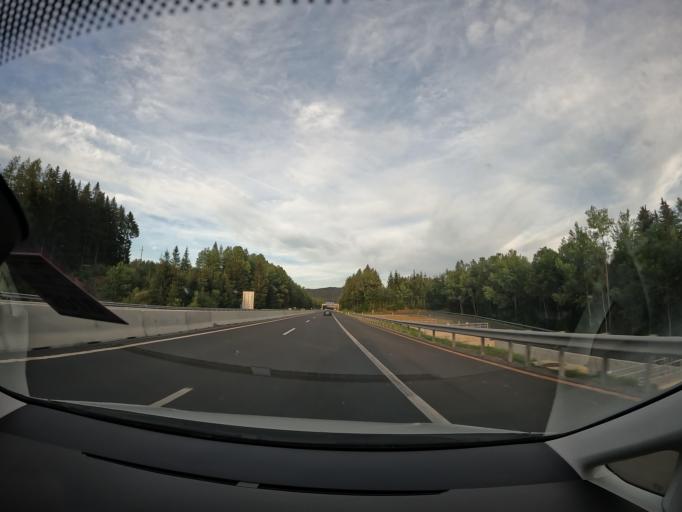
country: AT
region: Carinthia
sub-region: Politischer Bezirk Wolfsberg
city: Preitenegg
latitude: 46.9668
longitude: 14.9417
